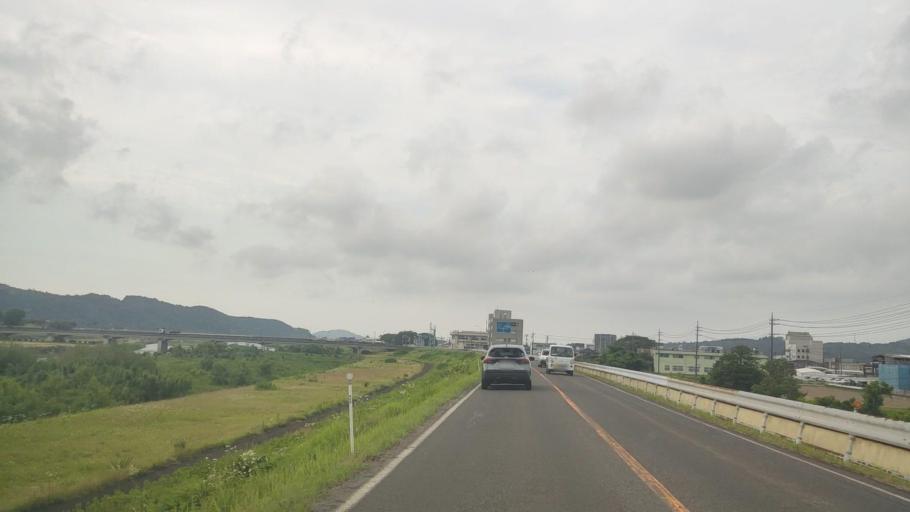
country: JP
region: Tottori
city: Kurayoshi
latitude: 35.4378
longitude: 133.8480
